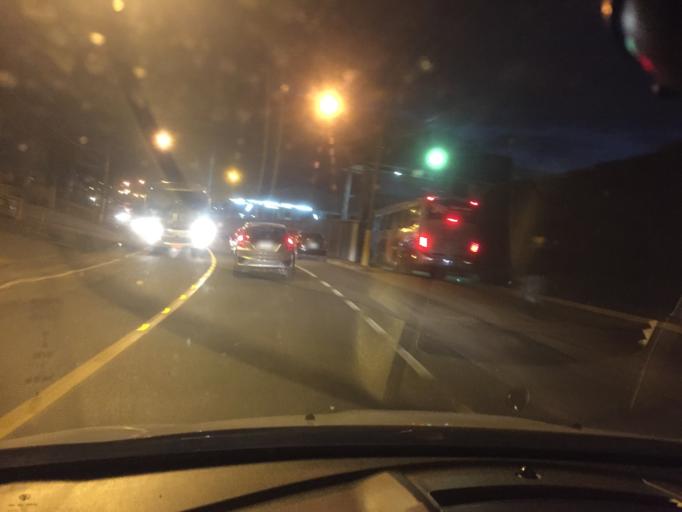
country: BR
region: Sao Paulo
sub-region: Campo Limpo Paulista
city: Campo Limpo Paulista
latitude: -23.2038
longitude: -46.7975
